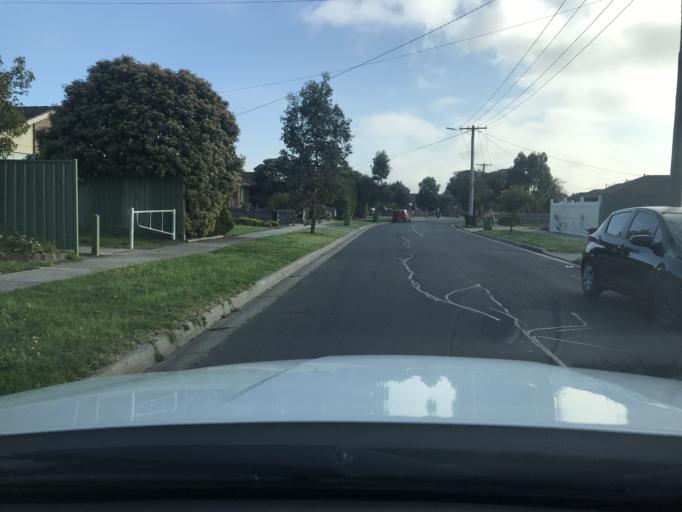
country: AU
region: Victoria
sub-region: Hume
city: Craigieburn
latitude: -37.6055
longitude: 144.9326
